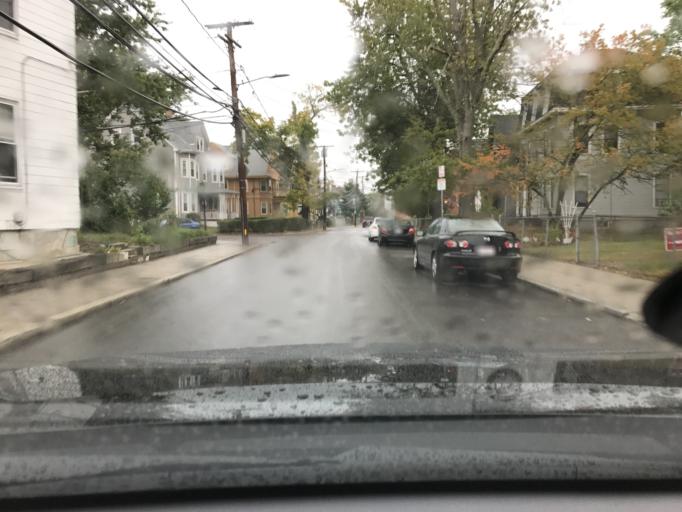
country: US
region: Massachusetts
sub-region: Norfolk County
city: Brookline
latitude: 42.3512
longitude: -71.1360
